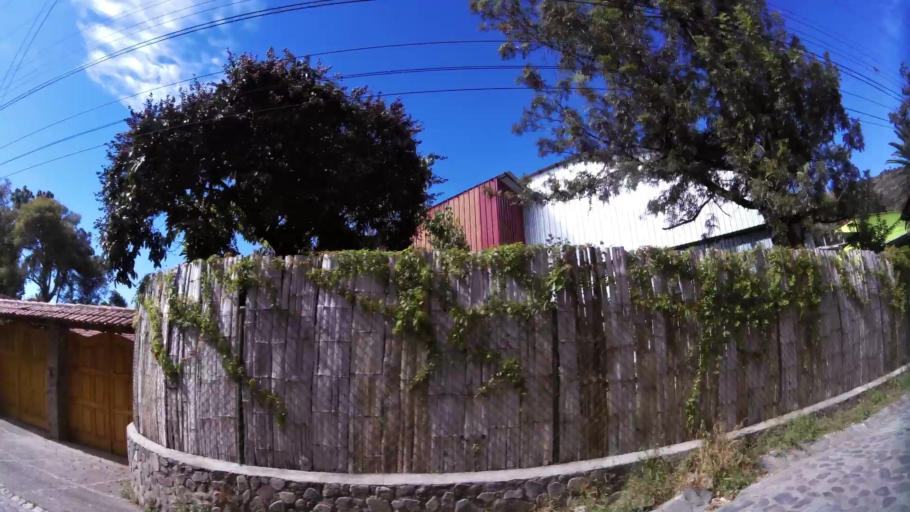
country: GT
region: Solola
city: Panajachel
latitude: 14.7421
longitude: -91.1552
